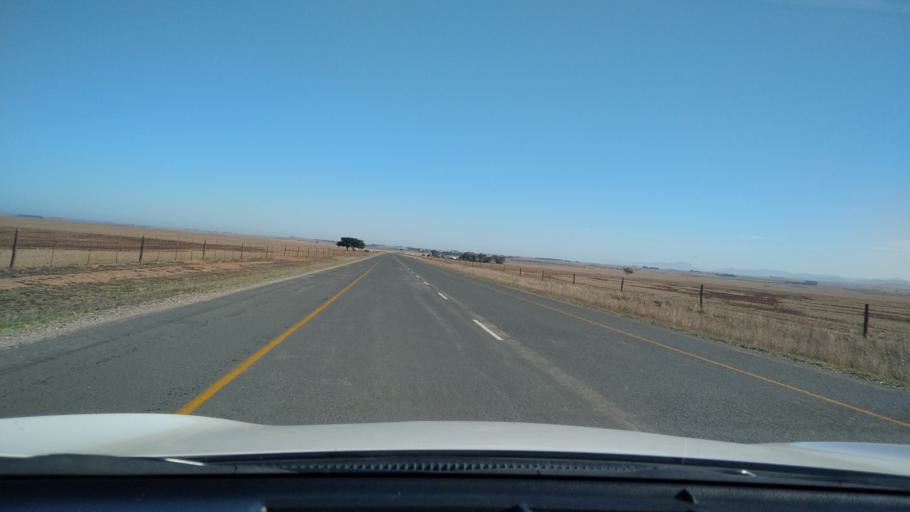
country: ZA
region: Western Cape
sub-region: West Coast District Municipality
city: Moorreesburg
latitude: -33.3168
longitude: 18.6234
